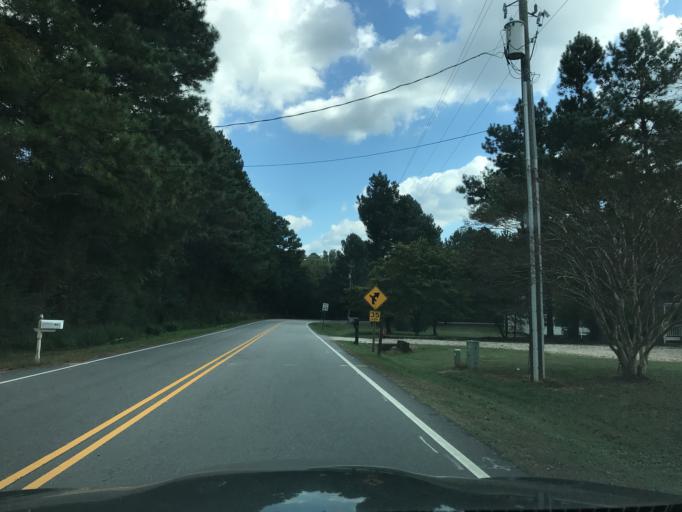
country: US
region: North Carolina
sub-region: Wake County
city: Wake Forest
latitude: 35.9340
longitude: -78.5312
